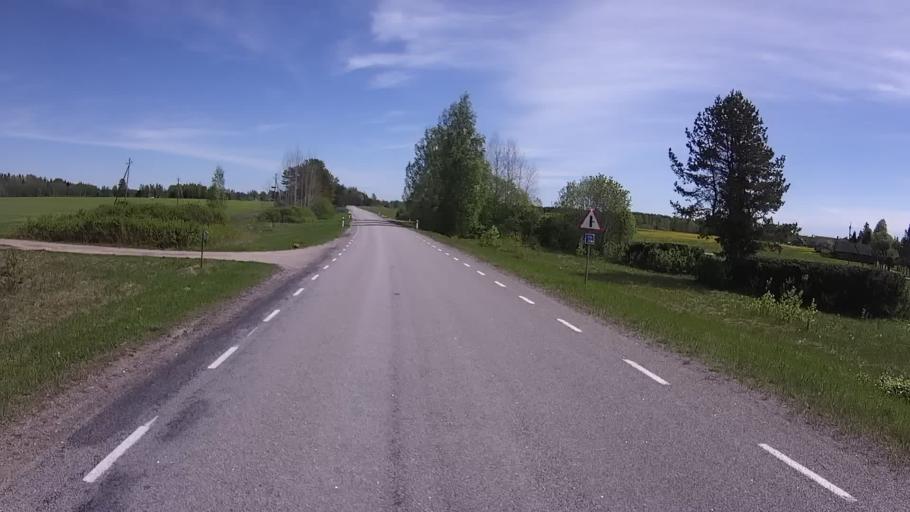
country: EE
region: Vorumaa
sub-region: Antsla vald
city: Vana-Antsla
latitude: 57.6144
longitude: 26.3640
